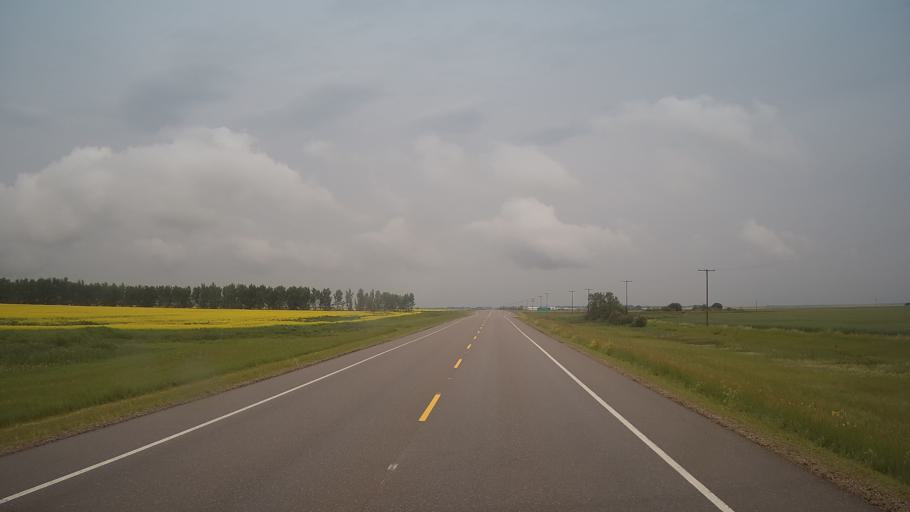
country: CA
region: Saskatchewan
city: Wilkie
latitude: 52.3438
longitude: -108.7137
